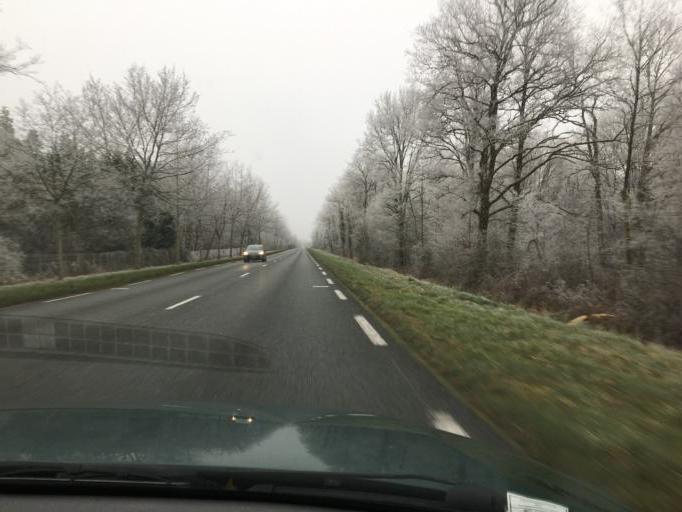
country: FR
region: Centre
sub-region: Departement du Loiret
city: La Ferte-Saint-Aubin
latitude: 47.7372
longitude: 1.9346
